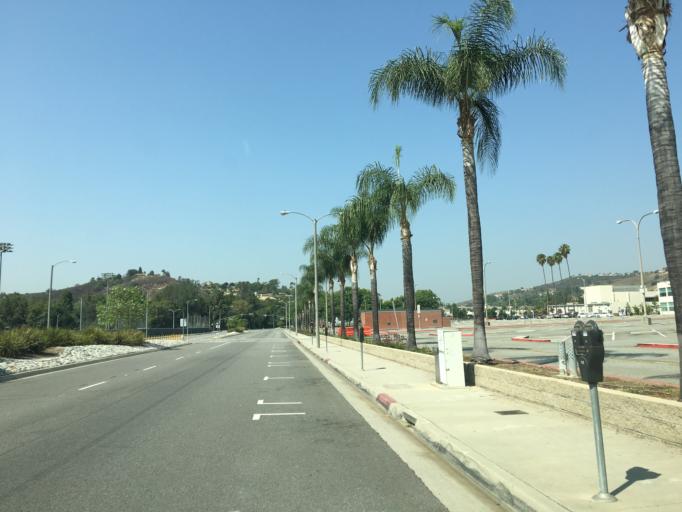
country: US
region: California
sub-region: Los Angeles County
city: Walnut
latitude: 34.0455
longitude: -117.8426
